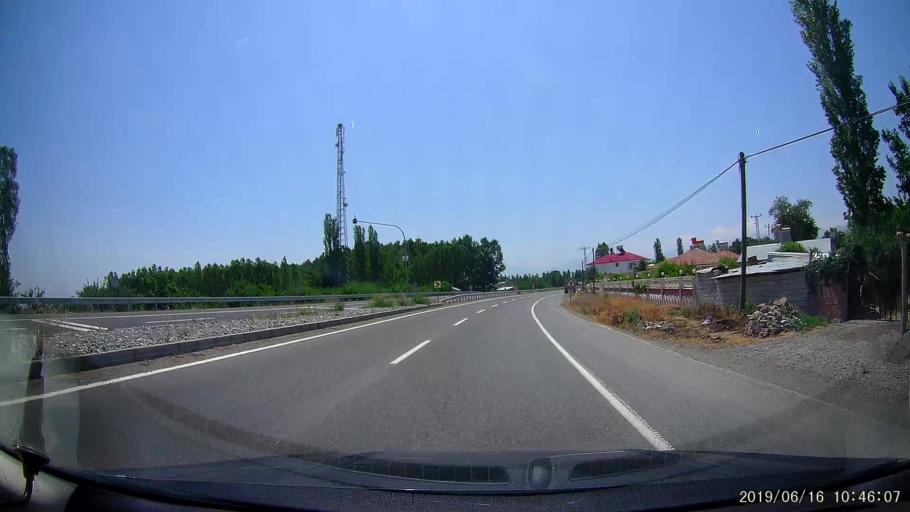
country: AM
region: Armavir
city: Shenavan
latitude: 40.0248
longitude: 43.8770
